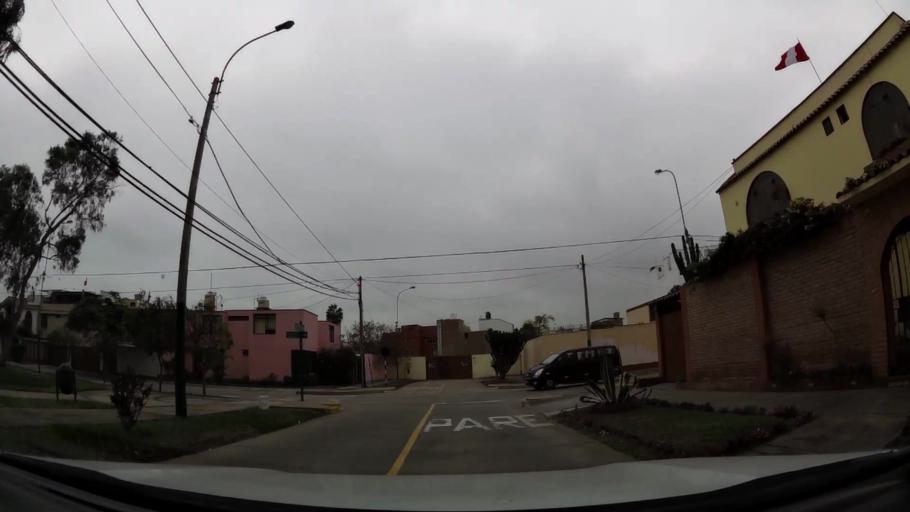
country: PE
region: Lima
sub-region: Lima
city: Surco
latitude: -12.1327
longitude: -77.0140
